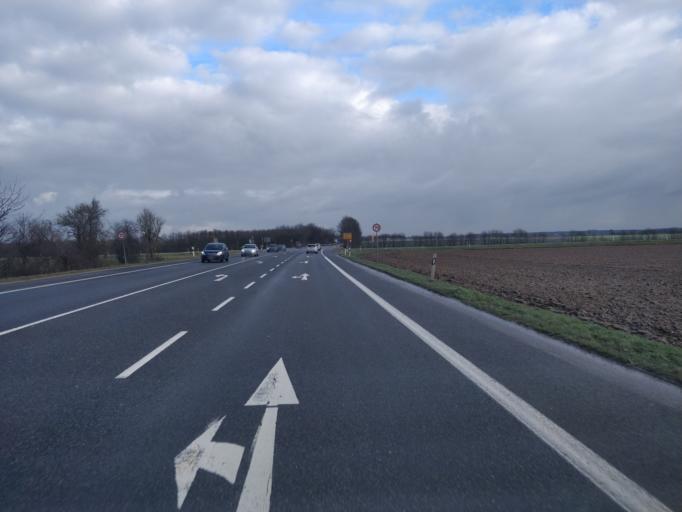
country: DE
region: North Rhine-Westphalia
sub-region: Regierungsbezirk Koln
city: Weilerswist
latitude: 50.7035
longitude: 6.8618
